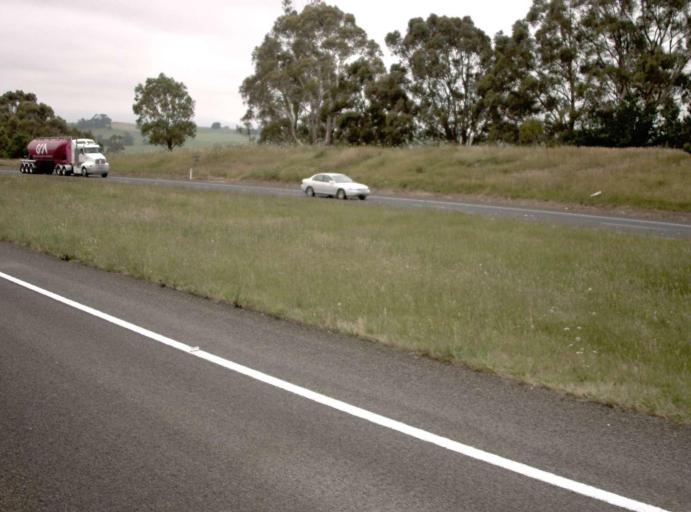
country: AU
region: Victoria
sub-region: Baw Baw
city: Warragul
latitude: -38.1347
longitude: 145.8808
